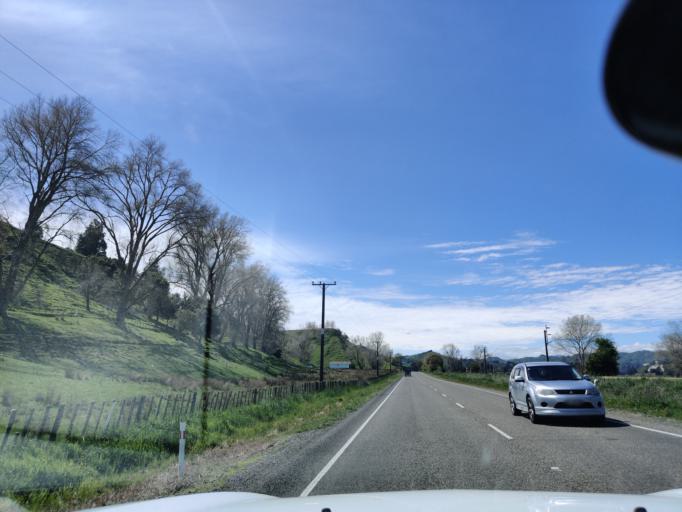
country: NZ
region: Manawatu-Wanganui
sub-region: Ruapehu District
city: Waiouru
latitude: -39.8540
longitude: 175.7276
